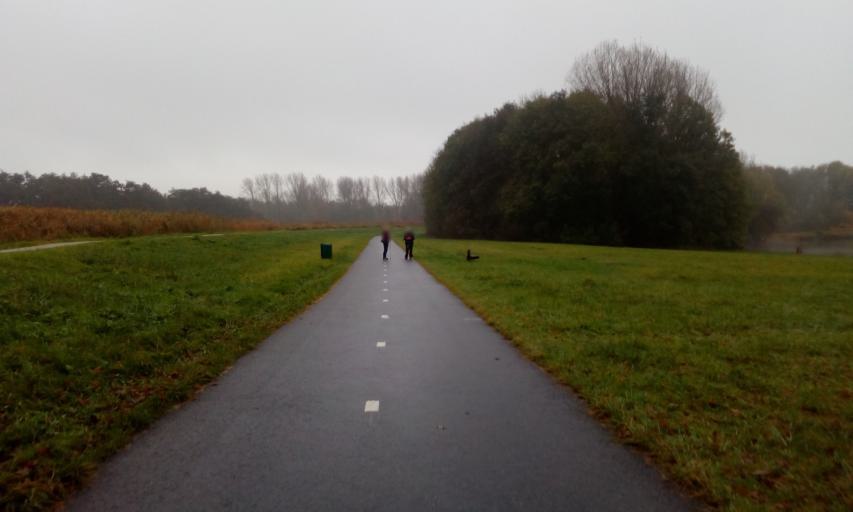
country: NL
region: South Holland
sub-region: Gemeente Lansingerland
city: Bleiswijk
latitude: 51.9966
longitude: 4.5489
